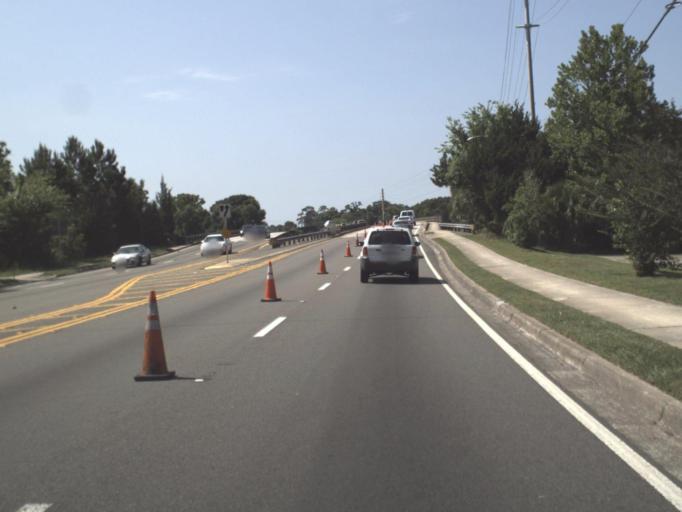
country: US
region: Florida
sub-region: Duval County
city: Jacksonville
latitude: 30.3977
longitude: -81.6833
